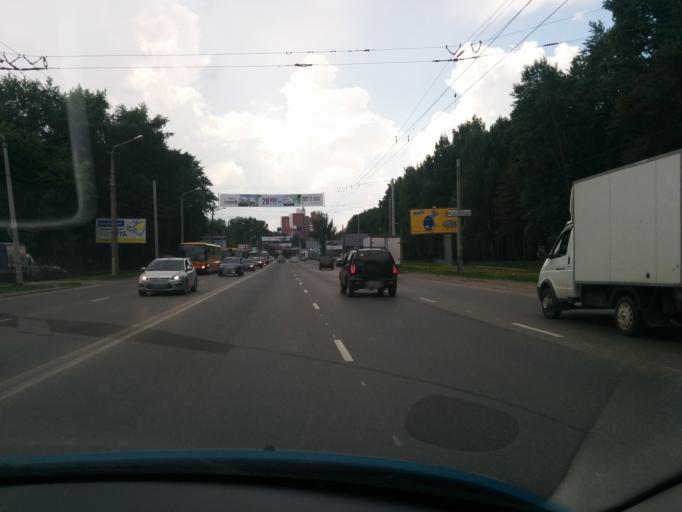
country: RU
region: Perm
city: Perm
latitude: 57.9842
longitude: 56.1826
